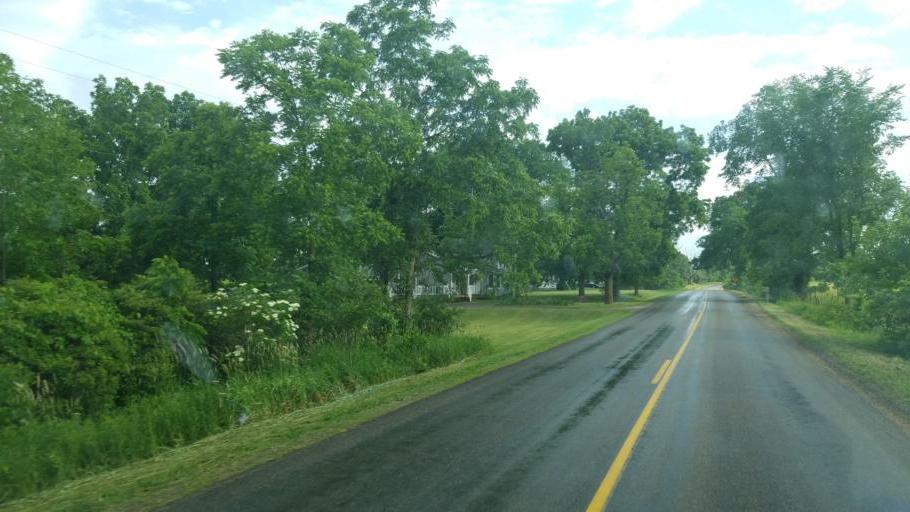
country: US
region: Michigan
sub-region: Eaton County
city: Bellevue
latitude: 42.5157
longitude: -85.0136
